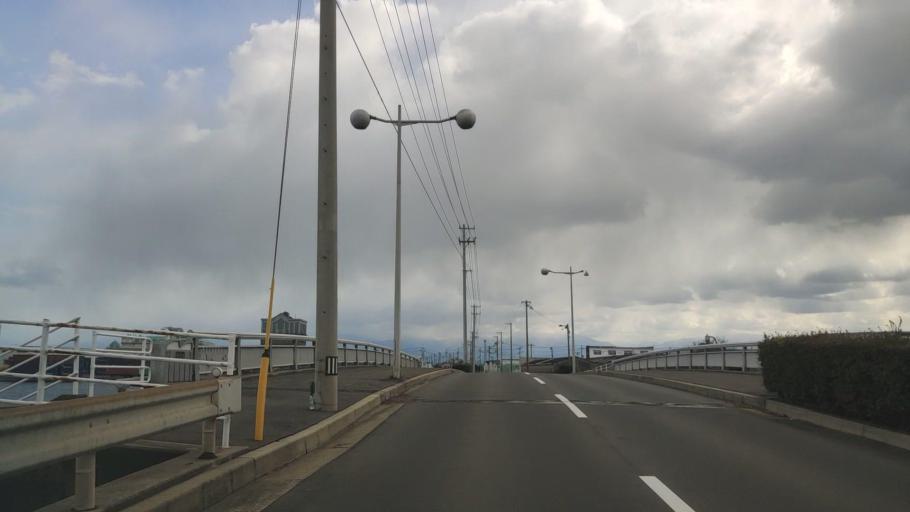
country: JP
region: Ehime
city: Saijo
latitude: 34.0519
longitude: 133.0234
